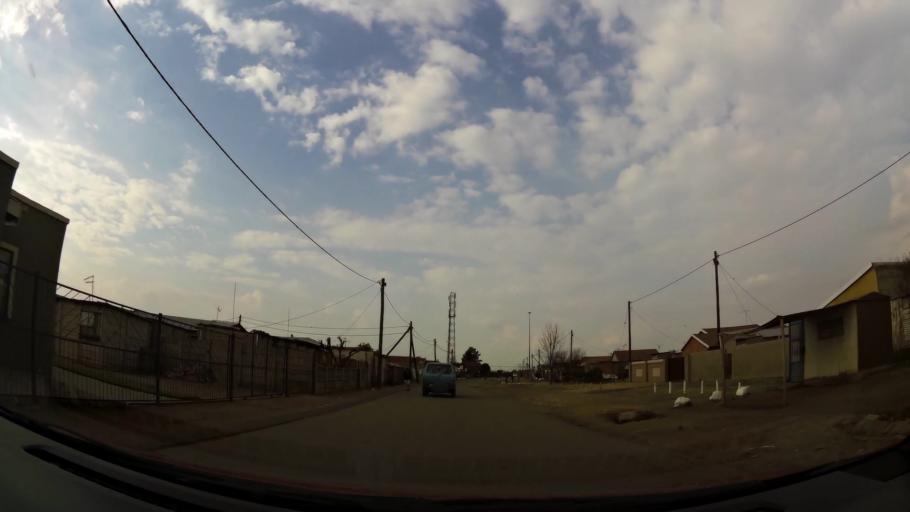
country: ZA
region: Gauteng
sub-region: Sedibeng District Municipality
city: Vanderbijlpark
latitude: -26.6740
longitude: 27.8732
